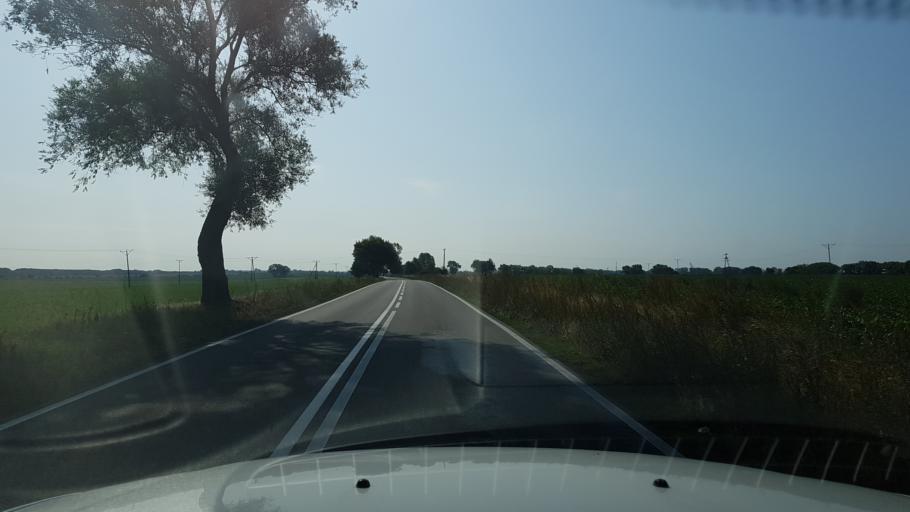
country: PL
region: West Pomeranian Voivodeship
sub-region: Powiat stargardzki
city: Stargard Szczecinski
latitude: 53.2656
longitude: 15.0916
